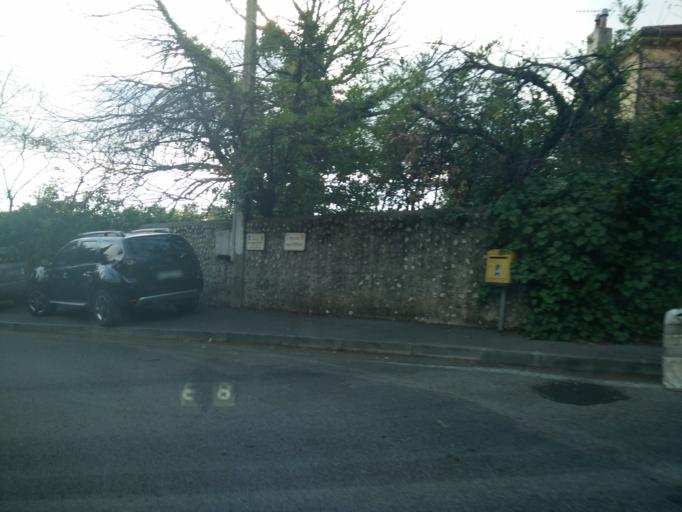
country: FR
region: Provence-Alpes-Cote d'Azur
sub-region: Departement des Alpes-Maritimes
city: Grasse
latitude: 43.6583
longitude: 6.9143
